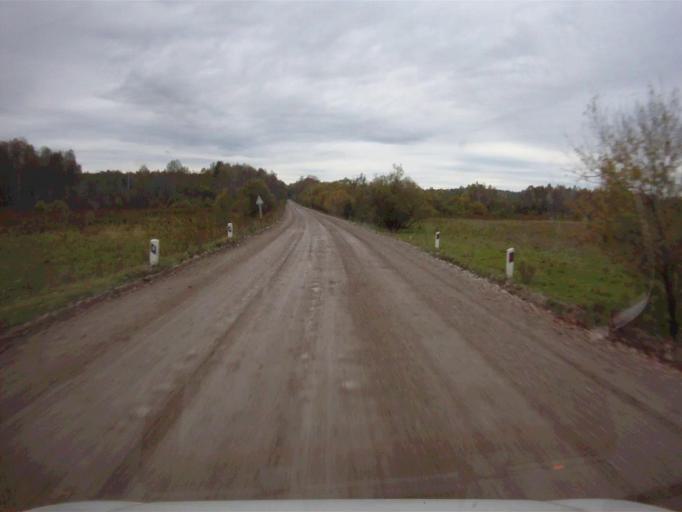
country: RU
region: Chelyabinsk
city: Nyazepetrovsk
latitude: 56.1258
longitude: 59.3501
